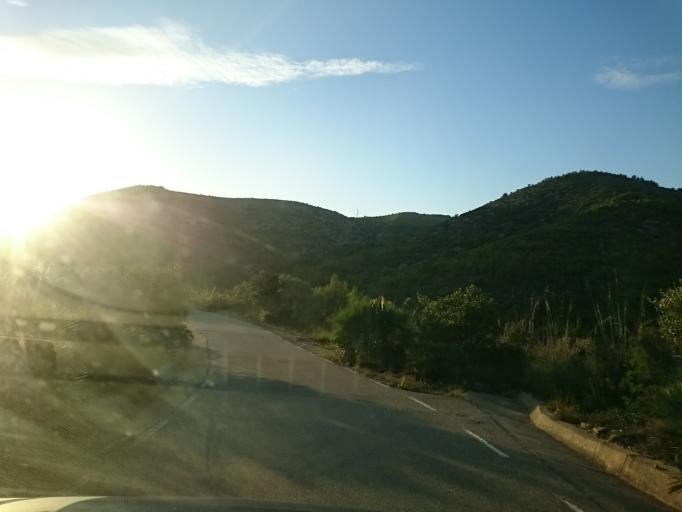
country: ES
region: Catalonia
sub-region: Provincia de Barcelona
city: Olivella
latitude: 41.3017
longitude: 1.8508
